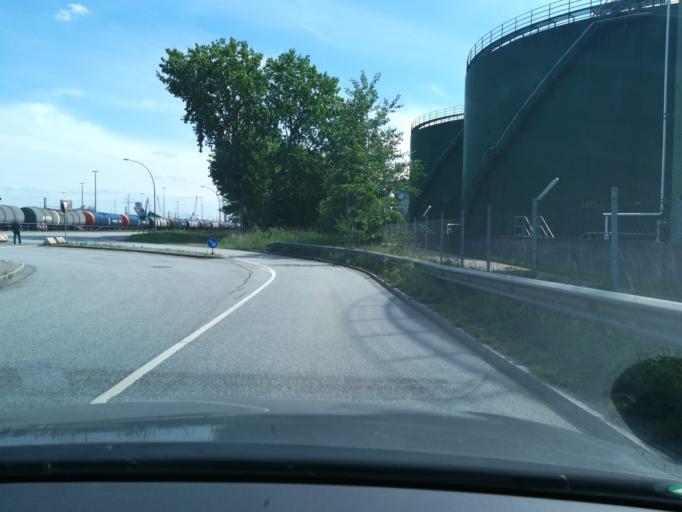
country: DE
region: Hamburg
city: Kleiner Grasbrook
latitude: 53.4995
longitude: 9.9689
